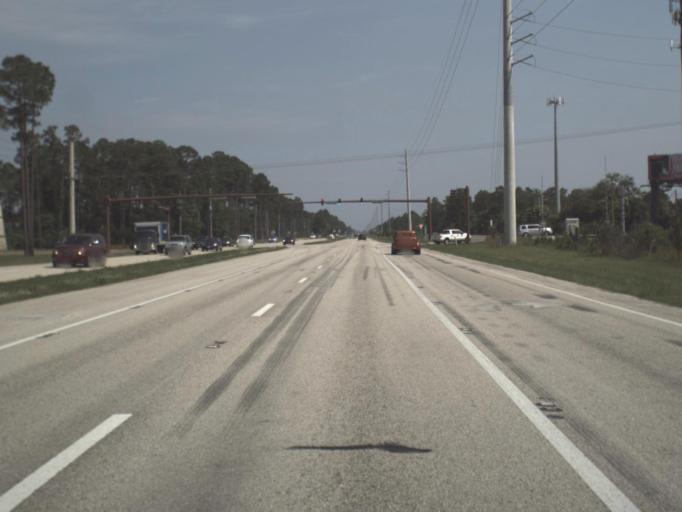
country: US
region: Florida
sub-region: Saint Johns County
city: Villano Beach
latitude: 30.0140
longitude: -81.3935
